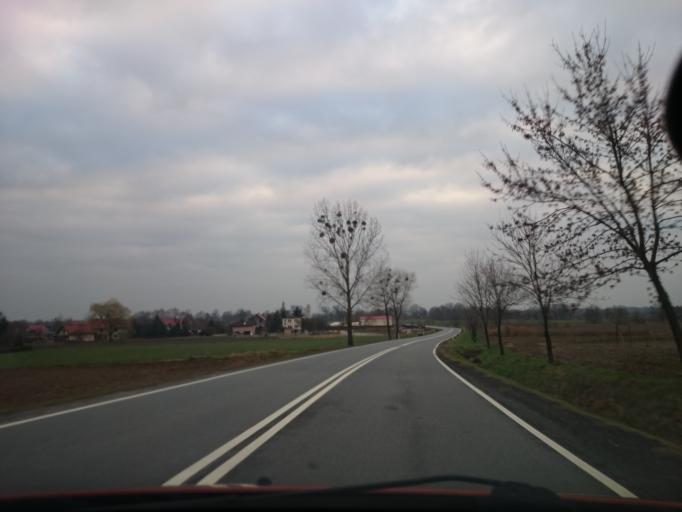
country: PL
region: Opole Voivodeship
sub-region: Powiat nyski
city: Sidzina
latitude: 50.5876
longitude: 17.4926
